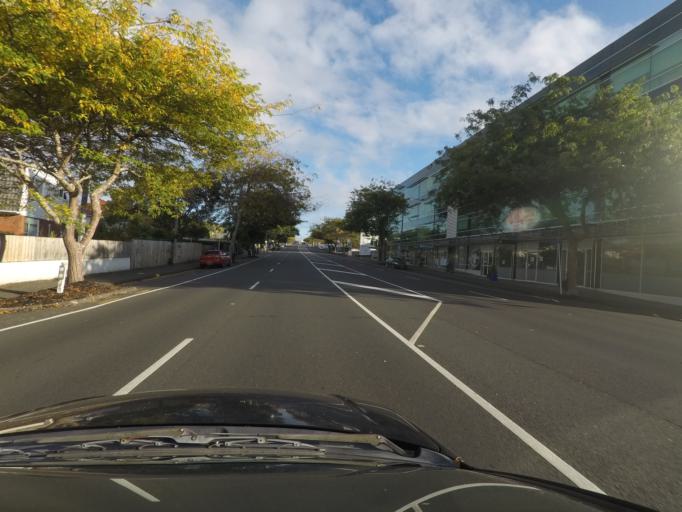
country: NZ
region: Auckland
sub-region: Auckland
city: Auckland
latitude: -36.8982
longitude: 174.8030
